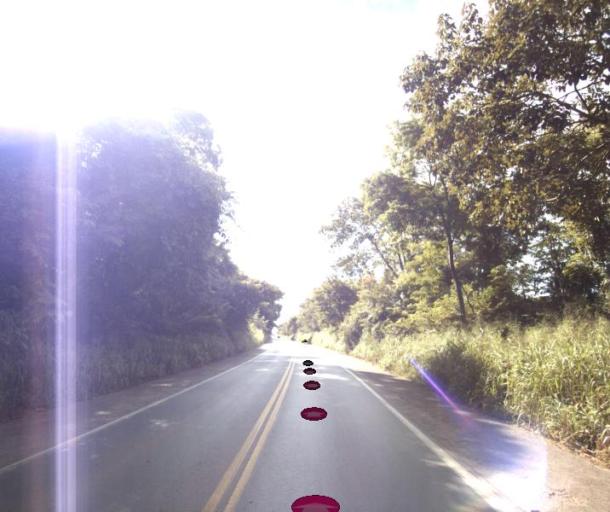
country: BR
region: Goias
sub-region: Jaragua
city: Jaragua
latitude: -15.7037
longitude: -49.3320
